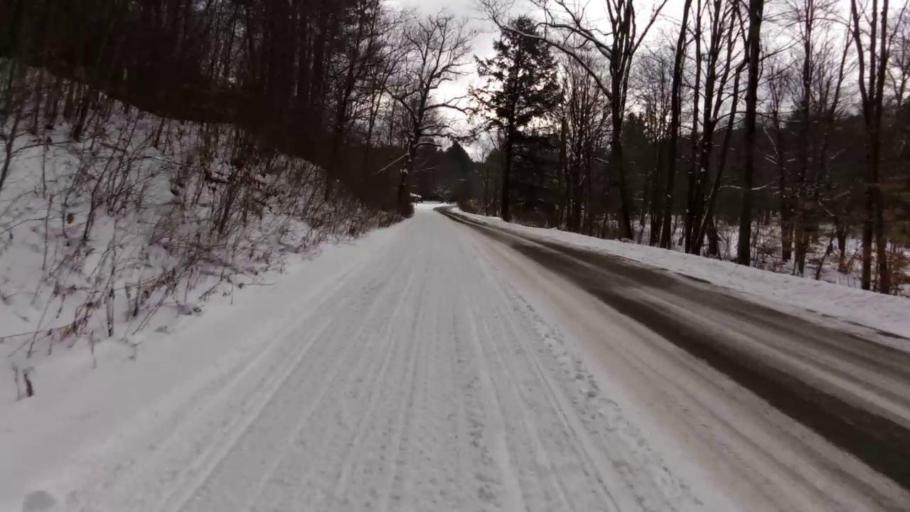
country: US
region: New York
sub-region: Cattaraugus County
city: Salamanca
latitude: 42.0937
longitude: -78.7473
